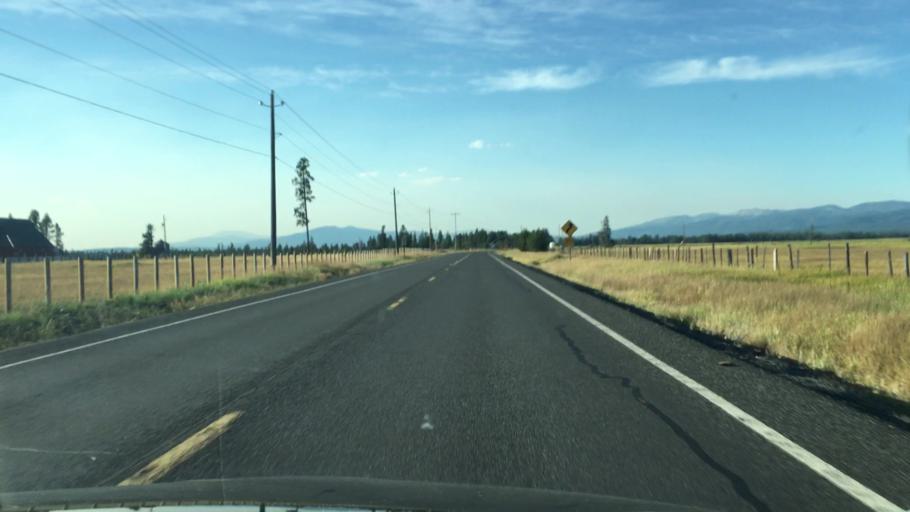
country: US
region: Idaho
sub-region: Valley County
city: McCall
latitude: 44.7690
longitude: -116.0781
